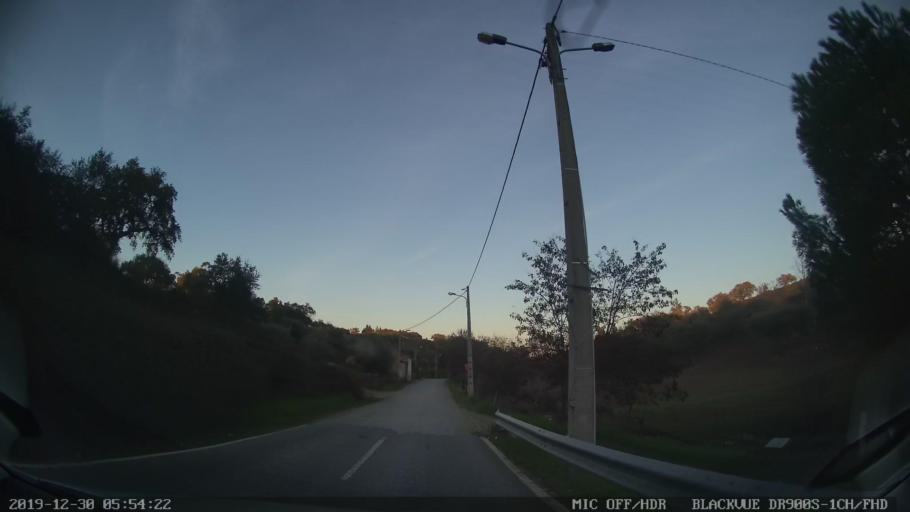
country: PT
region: Castelo Branco
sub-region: Idanha-A-Nova
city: Idanha-a-Nova
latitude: 40.0200
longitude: -7.2459
